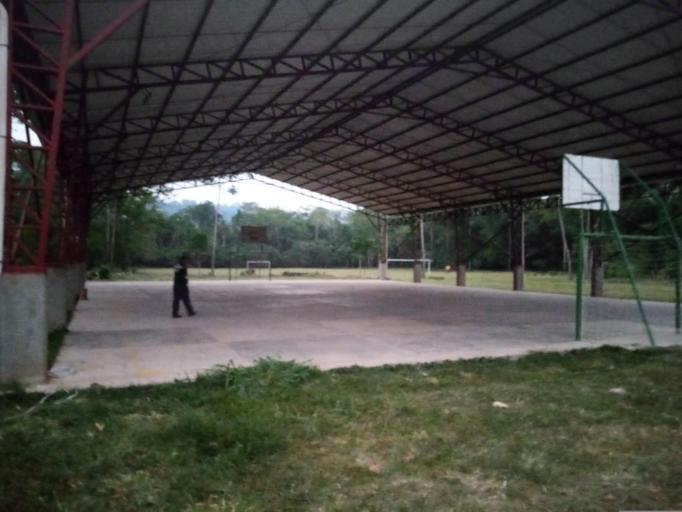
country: BO
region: La Paz
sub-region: Provincia Larecaja
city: Guanay
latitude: -15.5662
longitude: -67.3254
